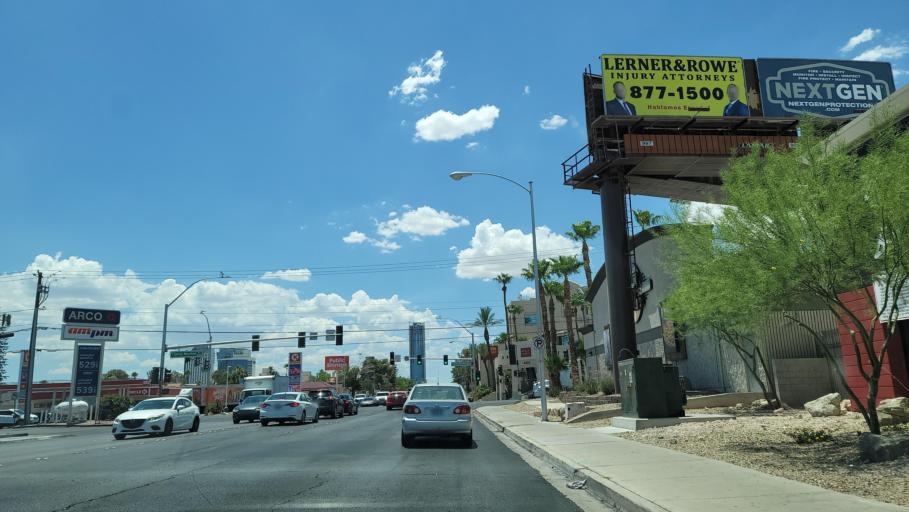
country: US
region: Nevada
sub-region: Clark County
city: Spring Valley
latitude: 36.1270
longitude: -115.1993
